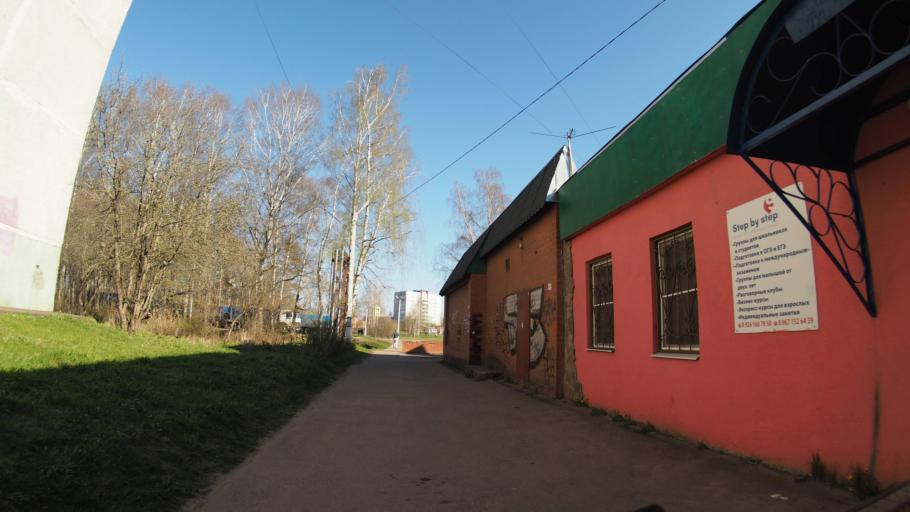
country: RU
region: Moskovskaya
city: Malyshevo
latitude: 55.5121
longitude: 38.3367
